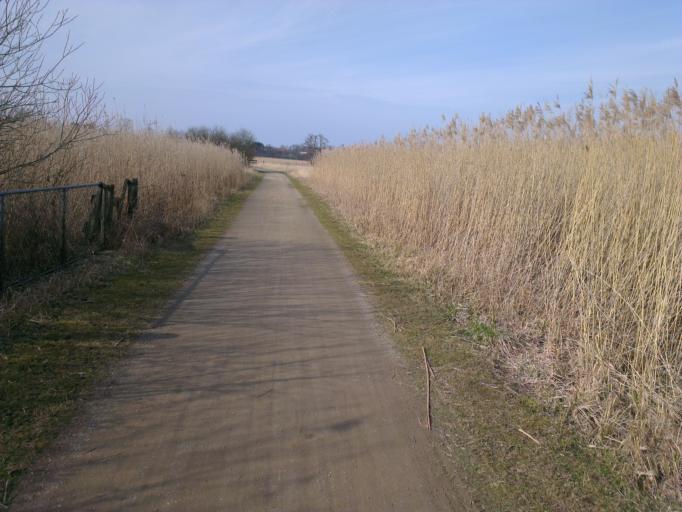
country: DK
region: Capital Region
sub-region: Frederikssund Kommune
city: Frederikssund
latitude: 55.8521
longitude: 12.0827
